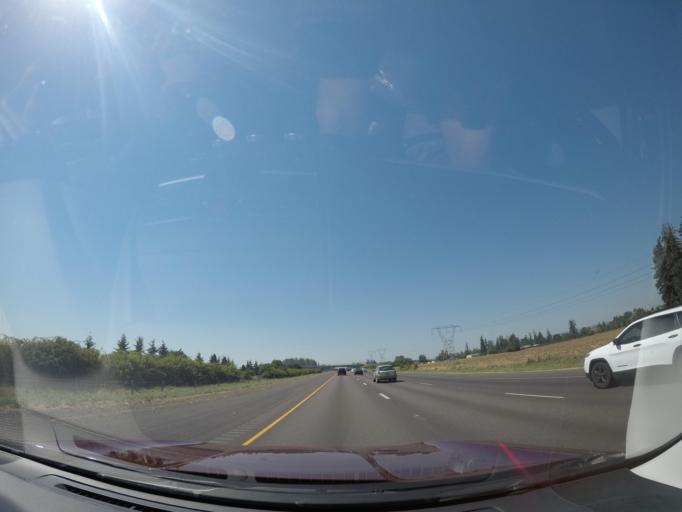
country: US
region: Oregon
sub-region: Marion County
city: Hayesville
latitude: 45.0320
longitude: -122.9833
